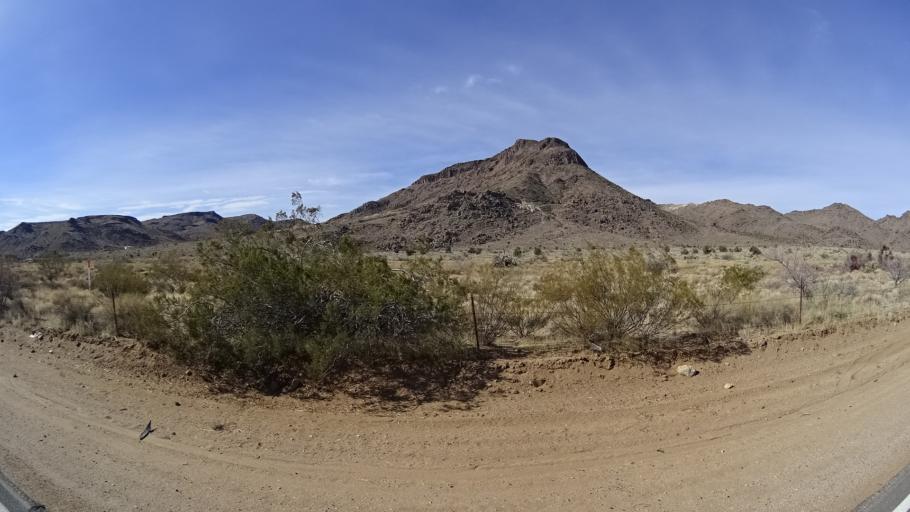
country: US
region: Arizona
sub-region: Mohave County
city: New Kingman-Butler
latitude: 35.2788
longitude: -114.0504
